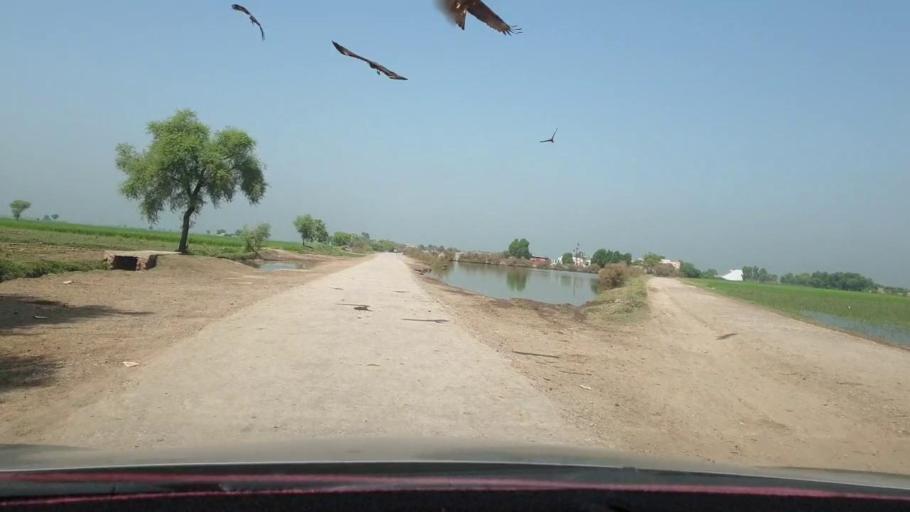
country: PK
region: Sindh
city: Kambar
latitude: 27.5987
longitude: 67.9832
